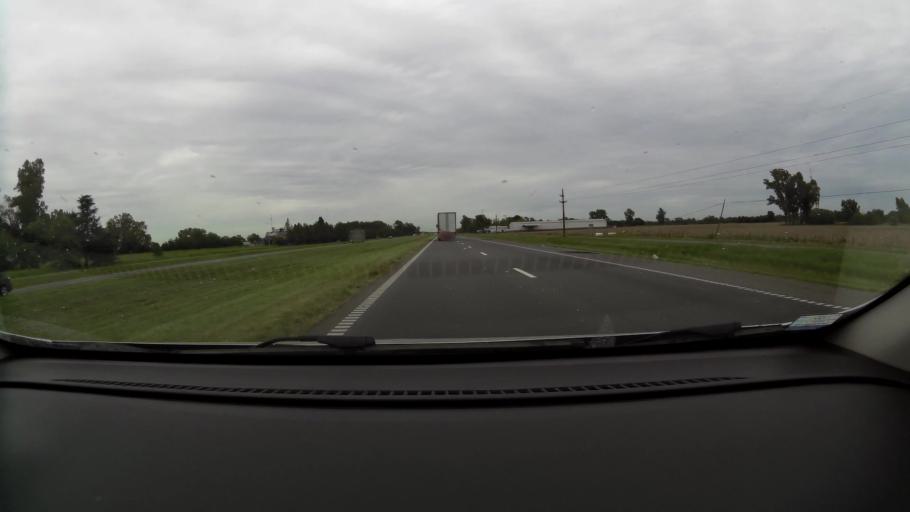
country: AR
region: Buenos Aires
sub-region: Partido de Zarate
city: Zarate
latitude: -34.0860
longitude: -59.1936
